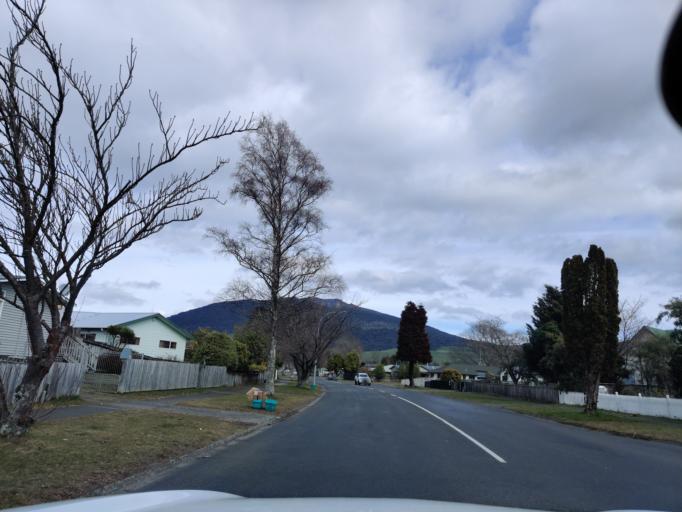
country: NZ
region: Waikato
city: Turangi
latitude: -38.9915
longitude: 175.8049
